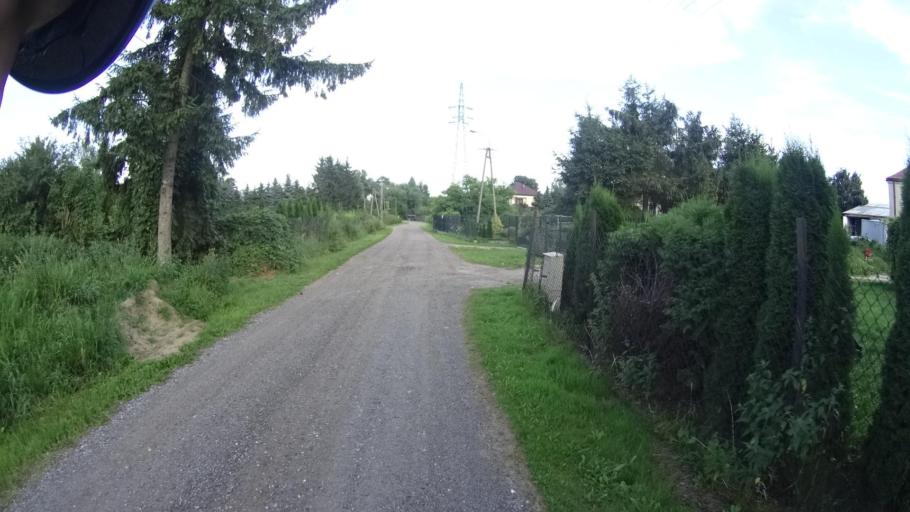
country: PL
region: Masovian Voivodeship
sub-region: Powiat piaseczynski
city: Tarczyn
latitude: 51.9768
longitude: 20.8416
